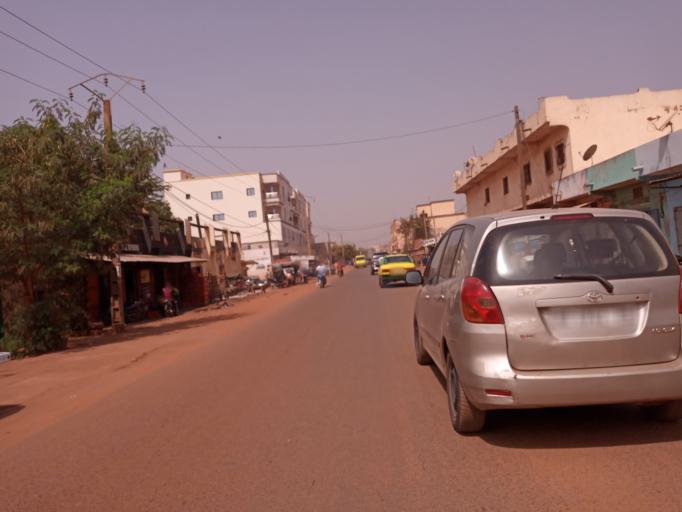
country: ML
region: Bamako
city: Bamako
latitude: 12.5888
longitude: -7.9795
